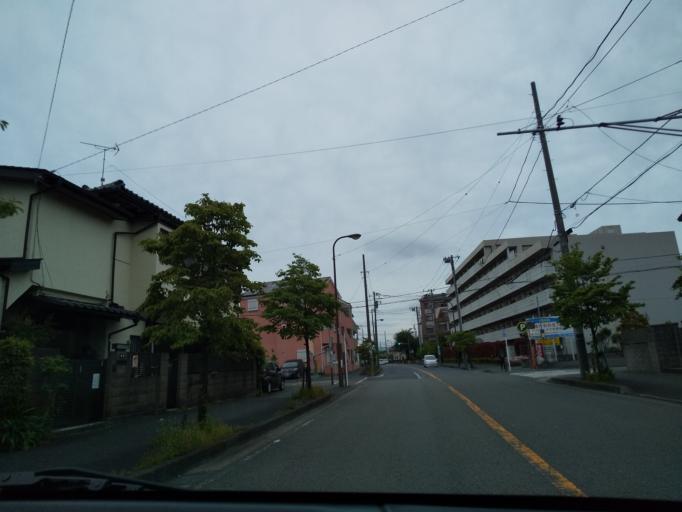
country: JP
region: Tokyo
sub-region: Machida-shi
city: Machida
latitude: 35.5507
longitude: 139.4160
